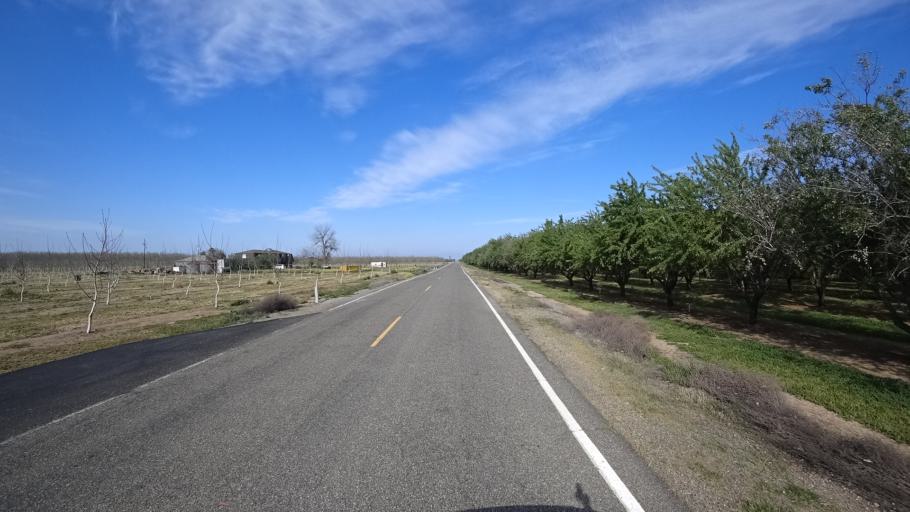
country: US
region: California
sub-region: Glenn County
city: Hamilton City
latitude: 39.6306
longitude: -122.0091
